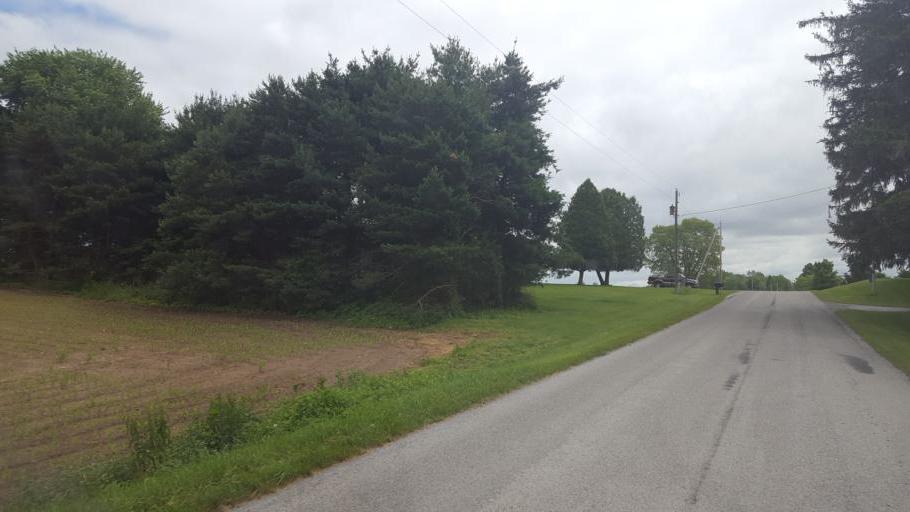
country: US
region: Ohio
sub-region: Crawford County
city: Bucyrus
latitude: 40.7754
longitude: -83.0802
